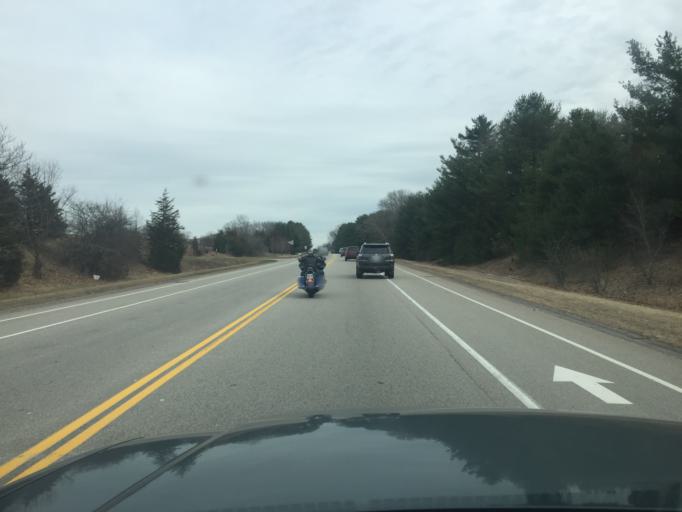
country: US
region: Massachusetts
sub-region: Norfolk County
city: Medfield
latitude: 42.1911
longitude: -71.3212
